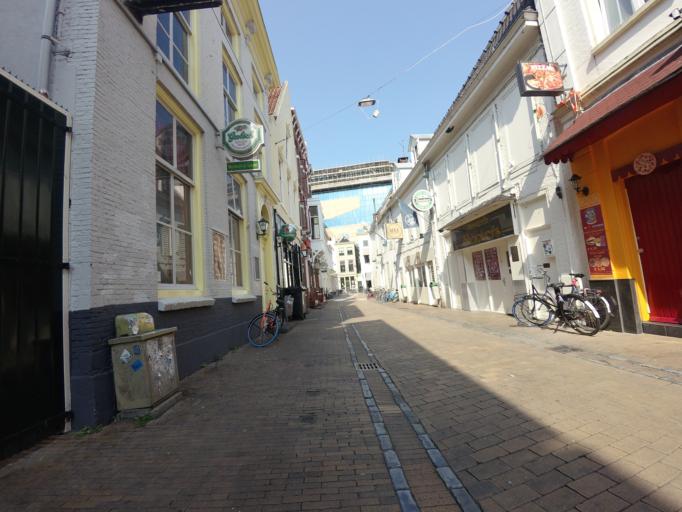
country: NL
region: Groningen
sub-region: Gemeente Groningen
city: Groningen
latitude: 53.2178
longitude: 6.5709
